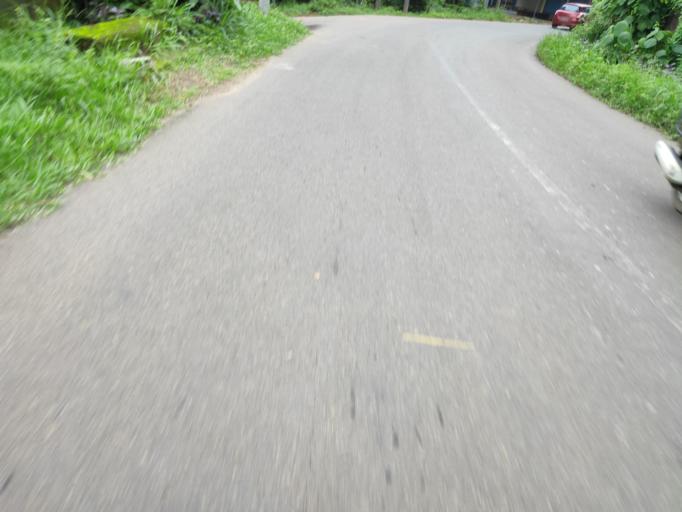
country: IN
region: Kerala
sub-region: Malappuram
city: Manjeri
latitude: 11.2212
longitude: 76.2639
